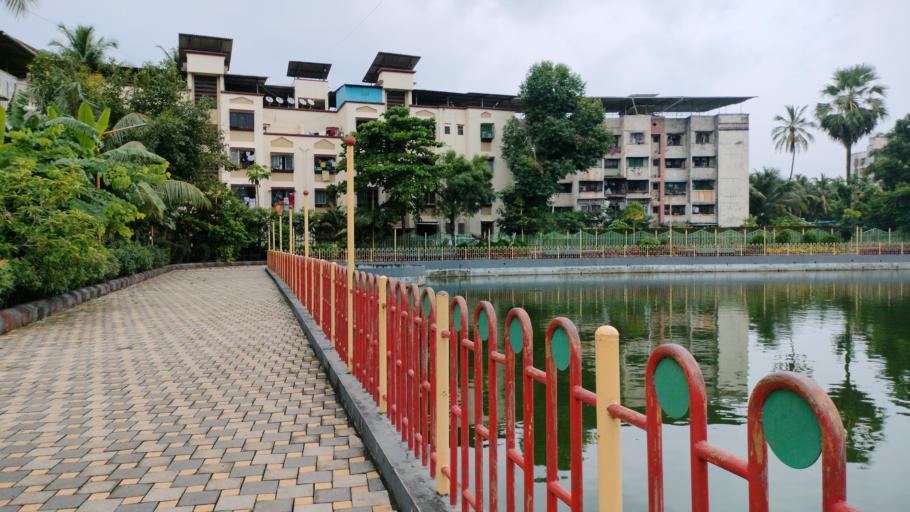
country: IN
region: Maharashtra
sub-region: Thane
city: Virar
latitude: 19.4422
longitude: 72.7950
